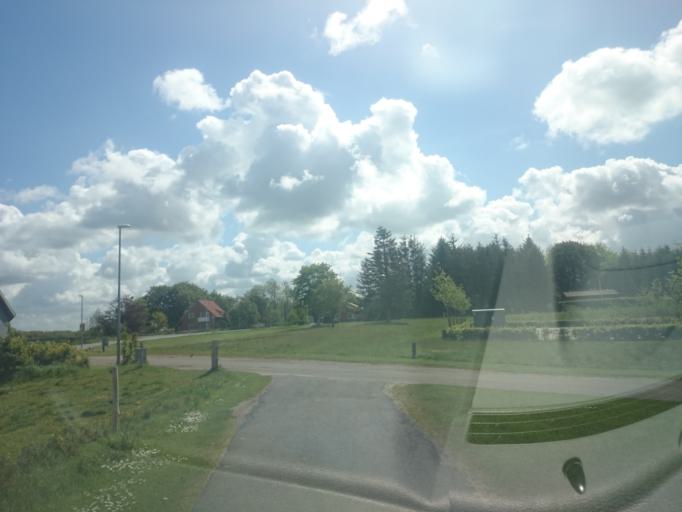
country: DK
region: South Denmark
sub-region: Billund Kommune
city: Grindsted
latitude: 55.6465
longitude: 8.8075
